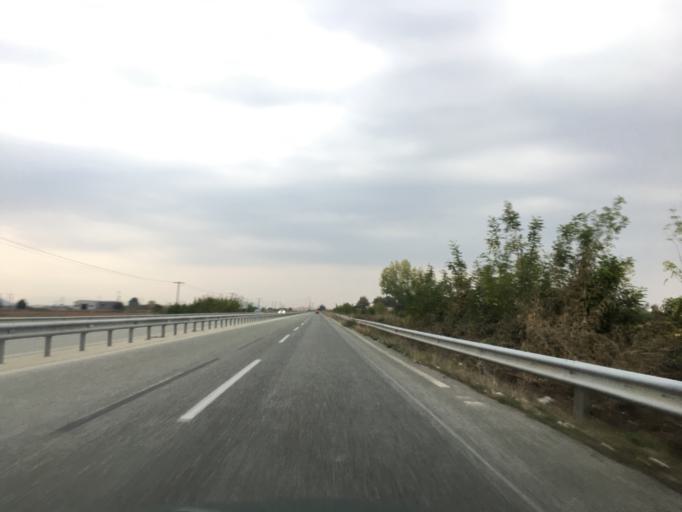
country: GR
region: Thessaly
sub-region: Trikala
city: Megalochori
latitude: 39.5648
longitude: 21.8500
